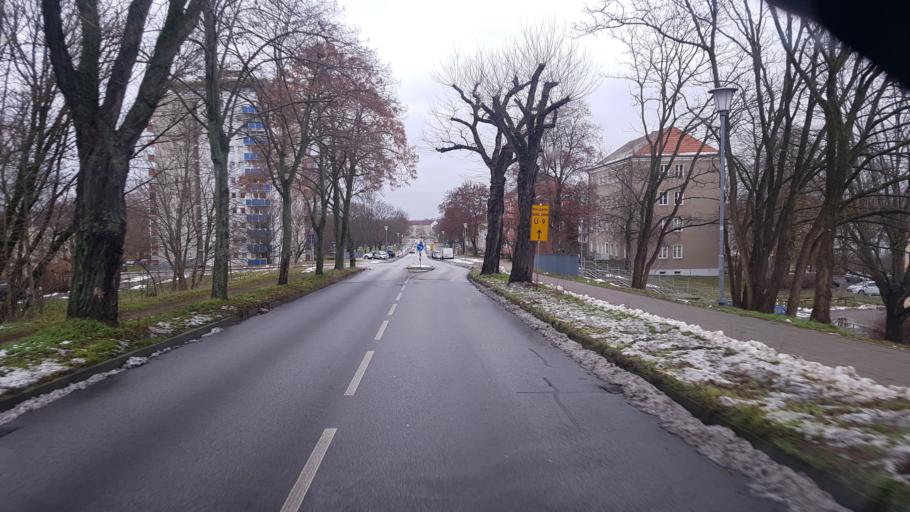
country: DE
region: Brandenburg
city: Eisenhuettenstadt
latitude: 52.1465
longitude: 14.6167
